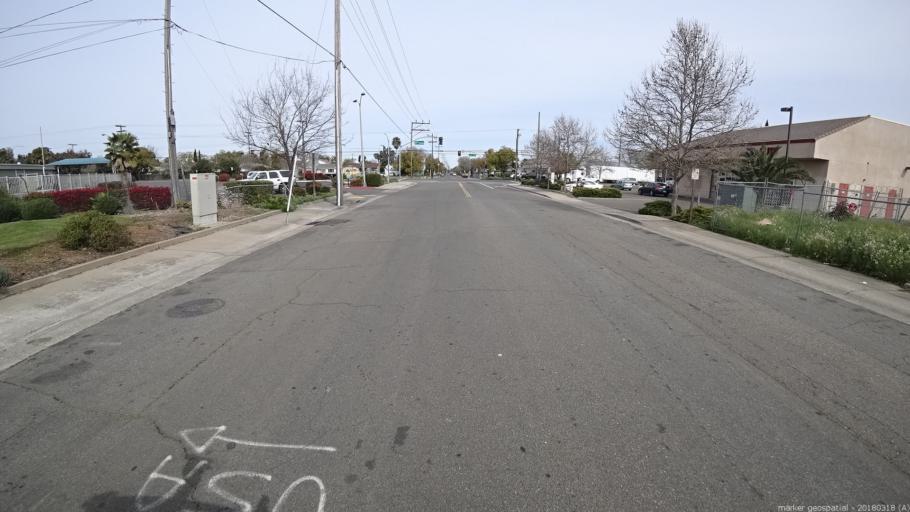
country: US
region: California
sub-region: Sacramento County
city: Parkway
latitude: 38.5098
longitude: -121.4554
